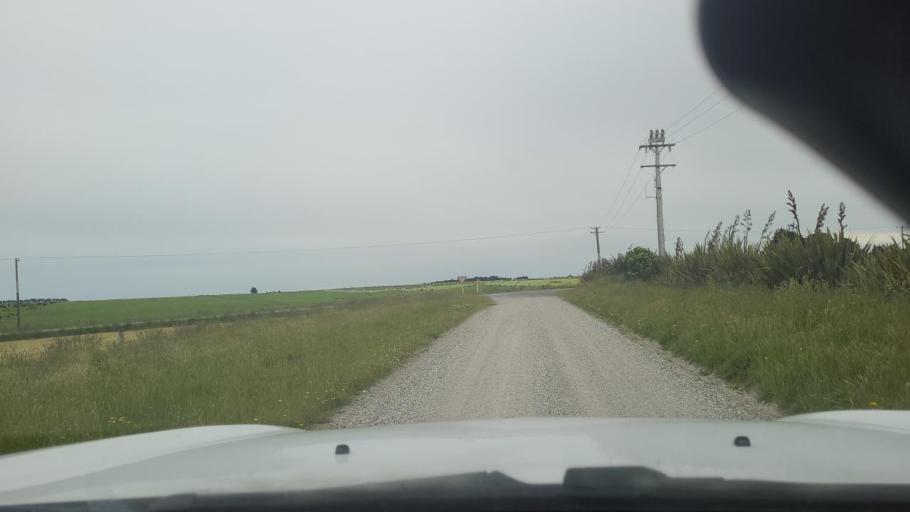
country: NZ
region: Southland
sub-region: Invercargill City
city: Invercargill
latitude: -46.4376
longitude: 168.5845
